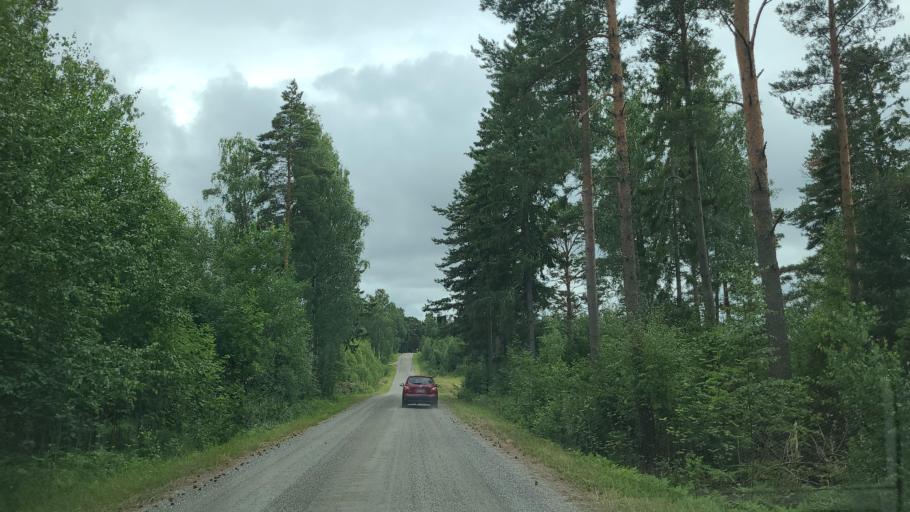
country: FI
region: Varsinais-Suomi
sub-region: Aboland-Turunmaa
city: Dragsfjaerd
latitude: 60.0873
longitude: 22.4159
